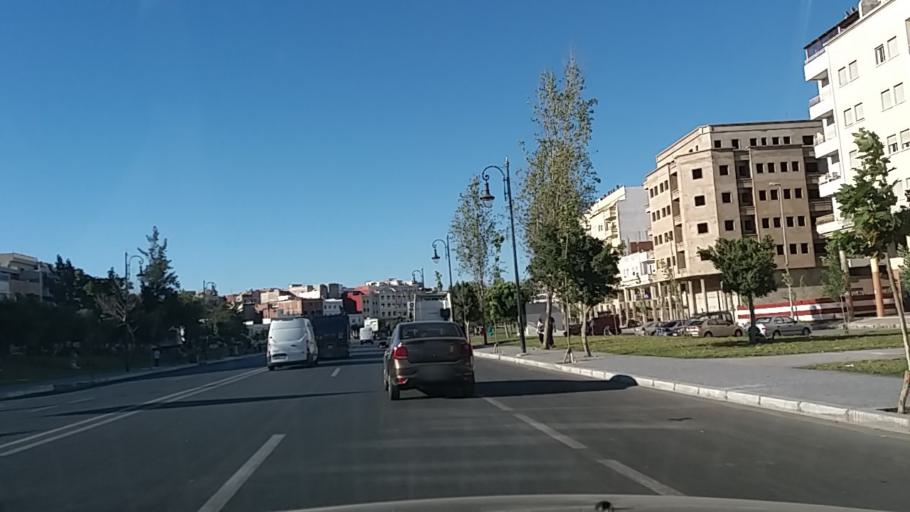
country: MA
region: Tanger-Tetouan
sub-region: Tanger-Assilah
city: Tangier
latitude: 35.7389
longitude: -5.8009
